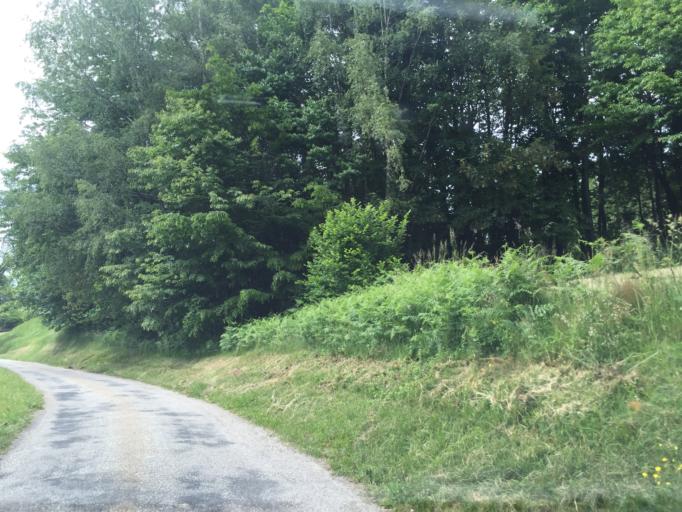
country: FR
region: Rhone-Alpes
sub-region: Departement de la Savoie
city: La Rochette
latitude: 45.4468
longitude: 6.1486
